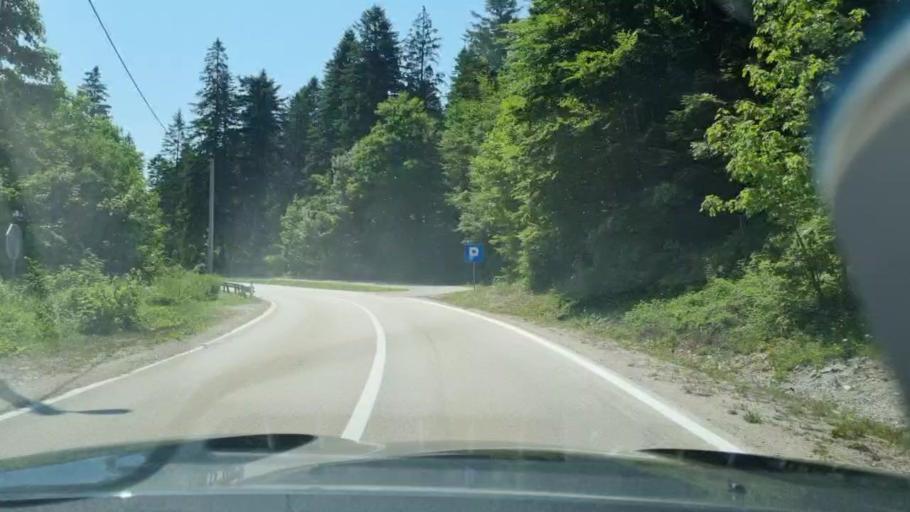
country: BA
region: Federation of Bosnia and Herzegovina
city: Sanica
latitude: 44.4810
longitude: 16.4041
